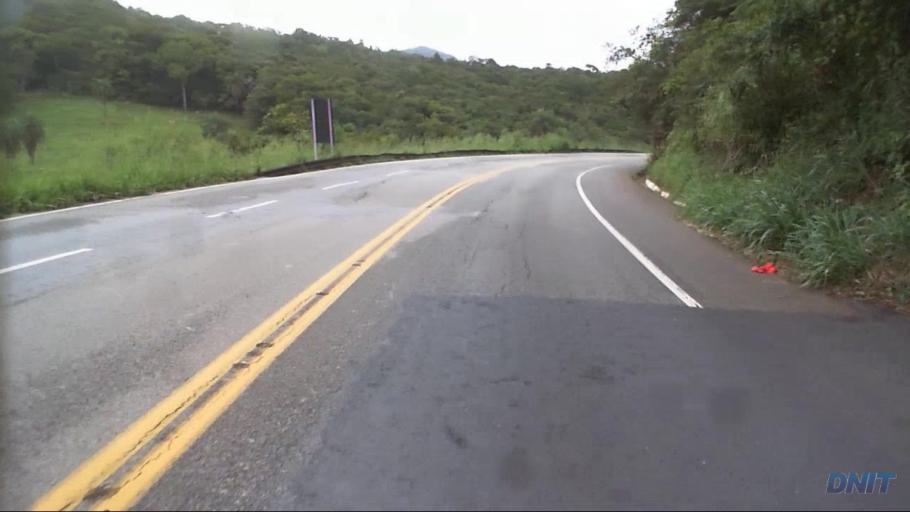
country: BR
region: Minas Gerais
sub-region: Joao Monlevade
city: Joao Monlevade
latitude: -19.8387
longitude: -43.3407
